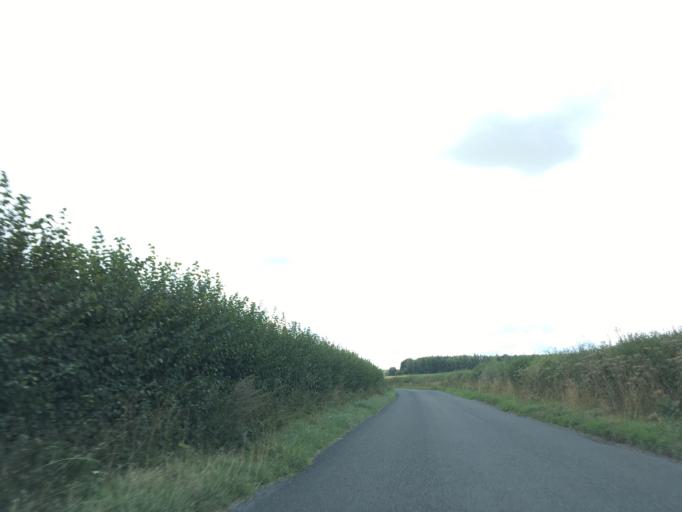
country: GB
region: England
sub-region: Hampshire
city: Kings Worthy
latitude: 51.1480
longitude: -1.3741
